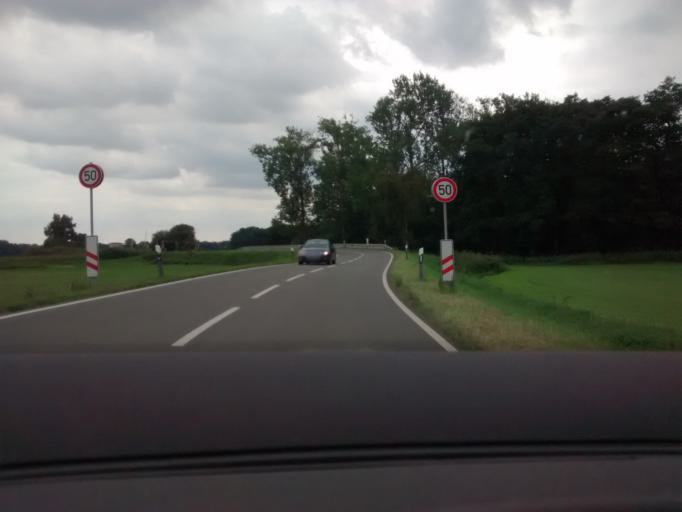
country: DE
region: Lower Saxony
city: Scharnebeck
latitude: 53.3195
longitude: 10.5059
